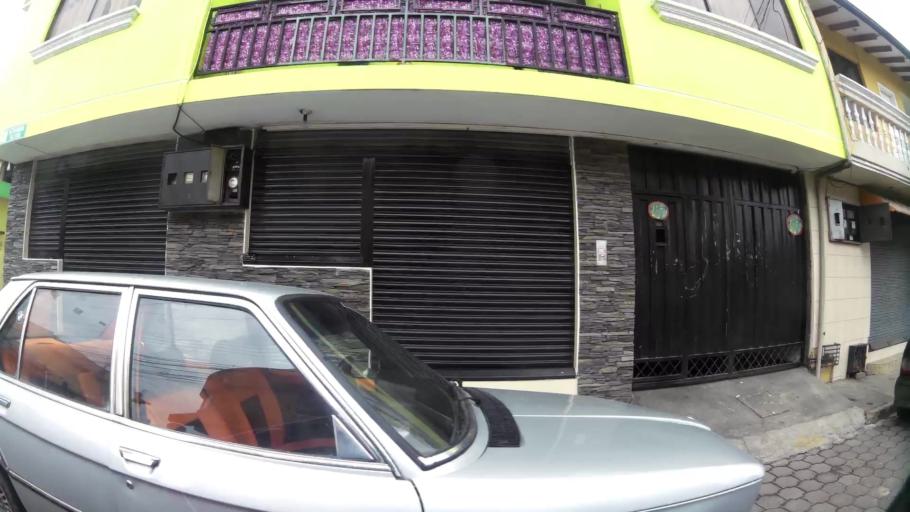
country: EC
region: Pichincha
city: Sangolqui
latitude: -0.3194
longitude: -78.4602
